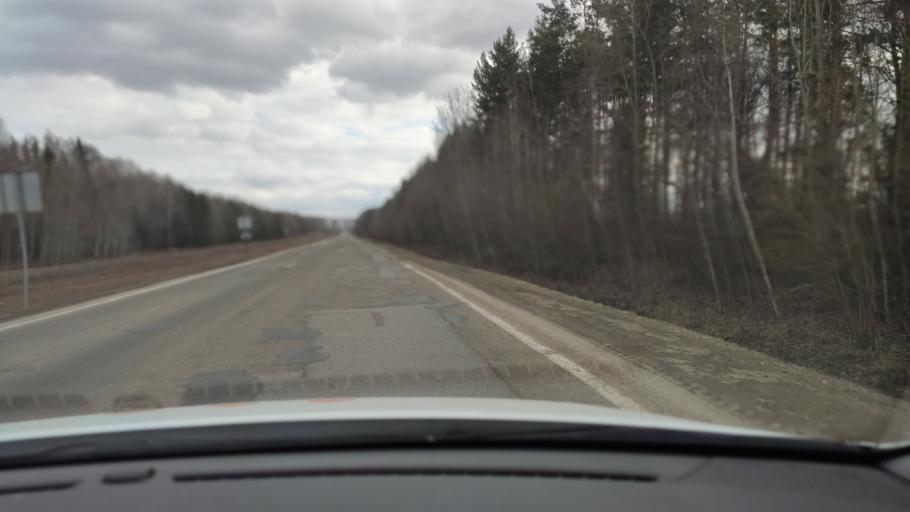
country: RU
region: Tatarstan
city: Vysokaya Gora
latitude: 56.1025
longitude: 49.1806
